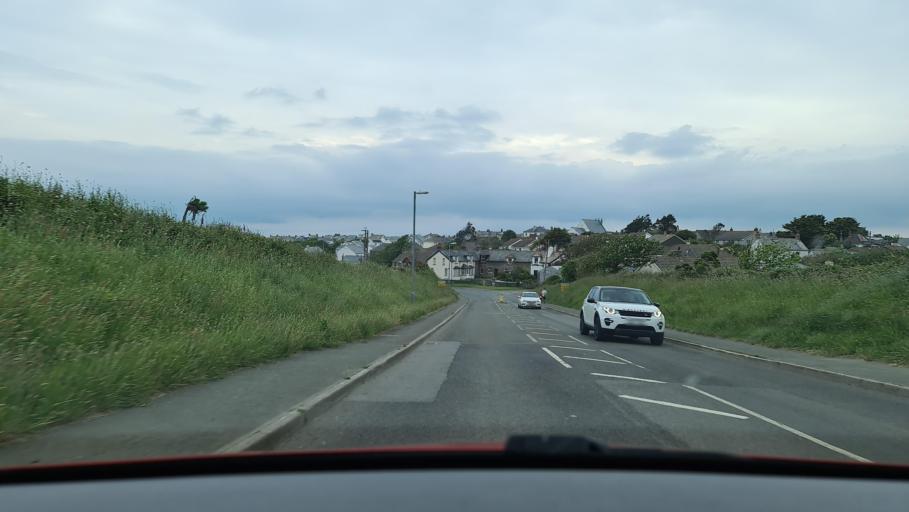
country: GB
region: England
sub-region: Cornwall
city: Tintagel
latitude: 50.6591
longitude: -4.7491
